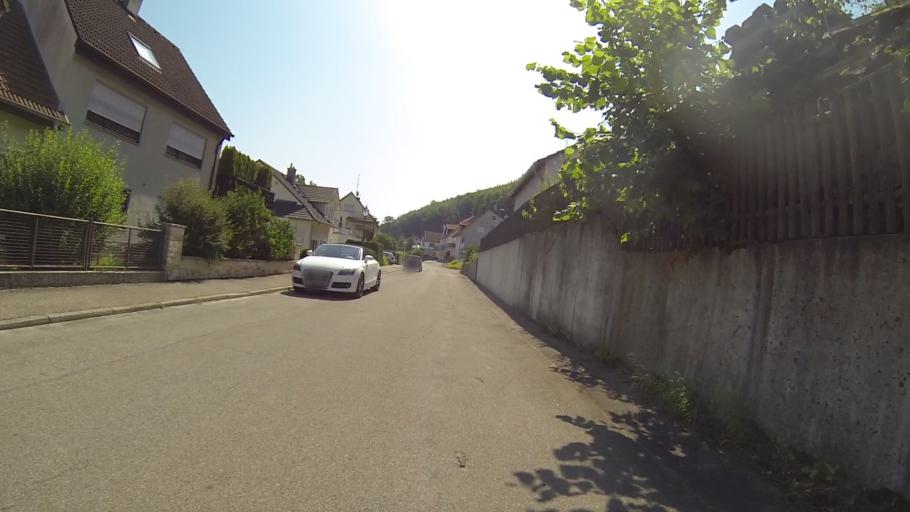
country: DE
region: Baden-Wuerttemberg
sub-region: Regierungsbezirk Stuttgart
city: Konigsbronn
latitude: 48.7347
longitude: 10.1188
